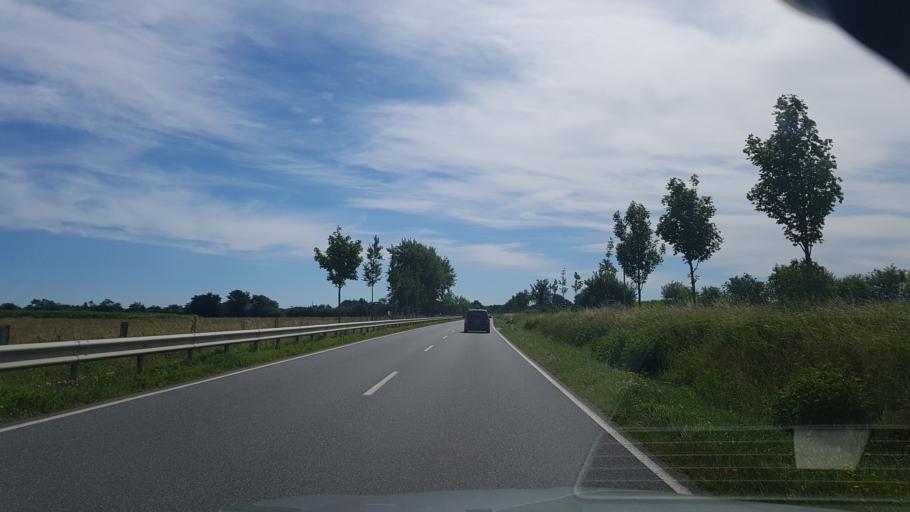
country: DE
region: Schleswig-Holstein
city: Wallsbull
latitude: 54.7984
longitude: 9.2794
